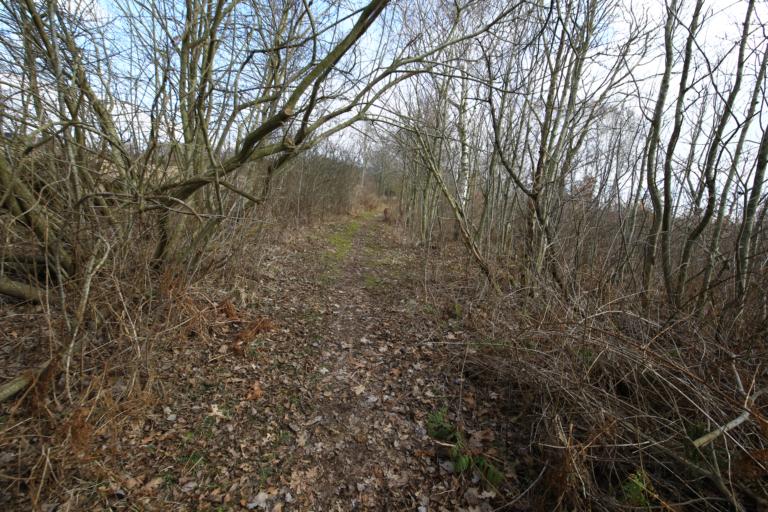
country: SE
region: Halland
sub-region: Kungsbacka Kommun
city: Frillesas
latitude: 57.2235
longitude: 12.1342
